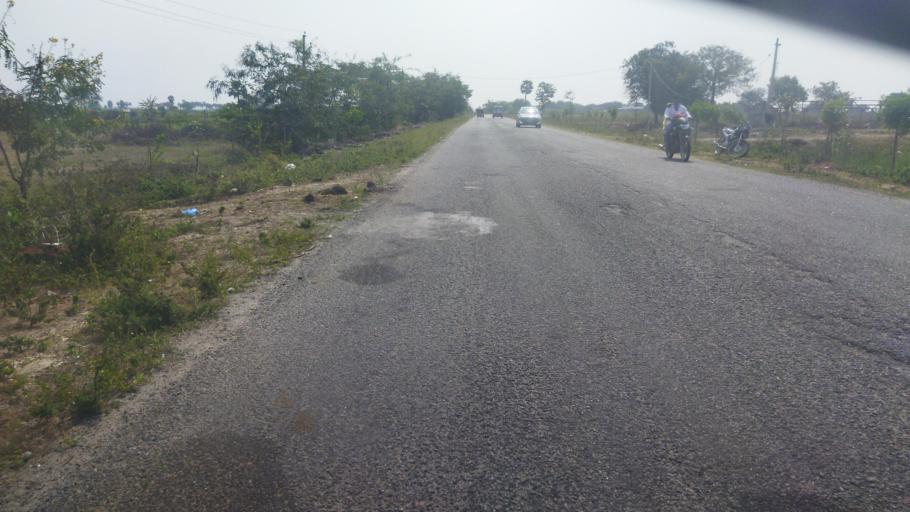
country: IN
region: Telangana
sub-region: Nalgonda
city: Nalgonda
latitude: 17.1006
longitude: 79.2843
